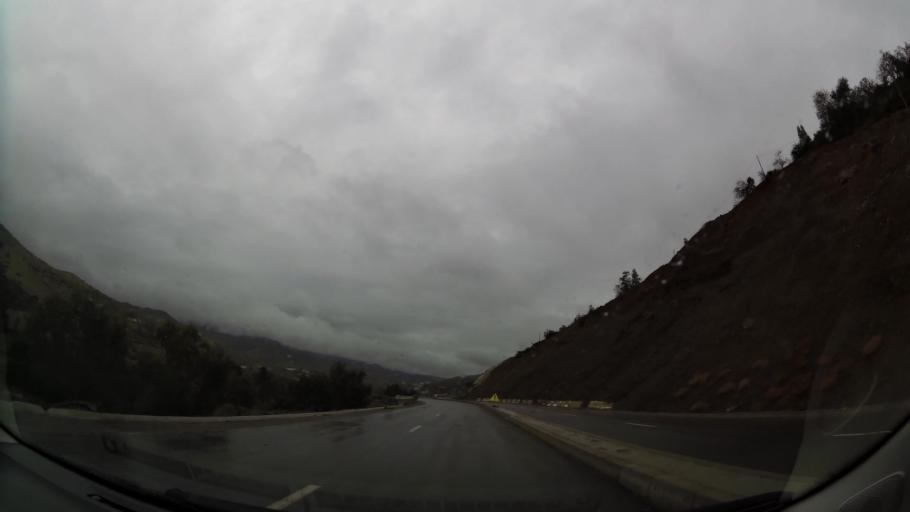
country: MA
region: Taza-Al Hoceima-Taounate
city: Imzourene
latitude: 35.0065
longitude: -3.8121
